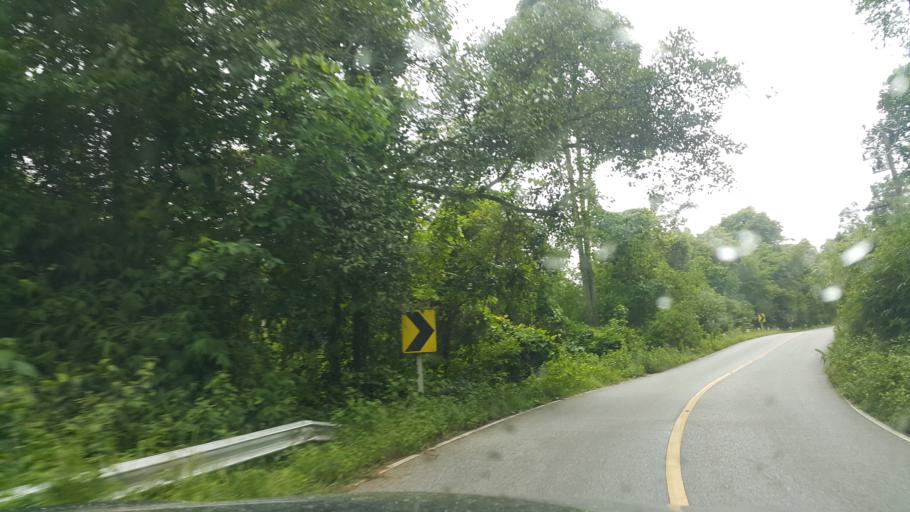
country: TH
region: Loei
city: Na Haeo
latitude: 17.5055
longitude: 100.8153
